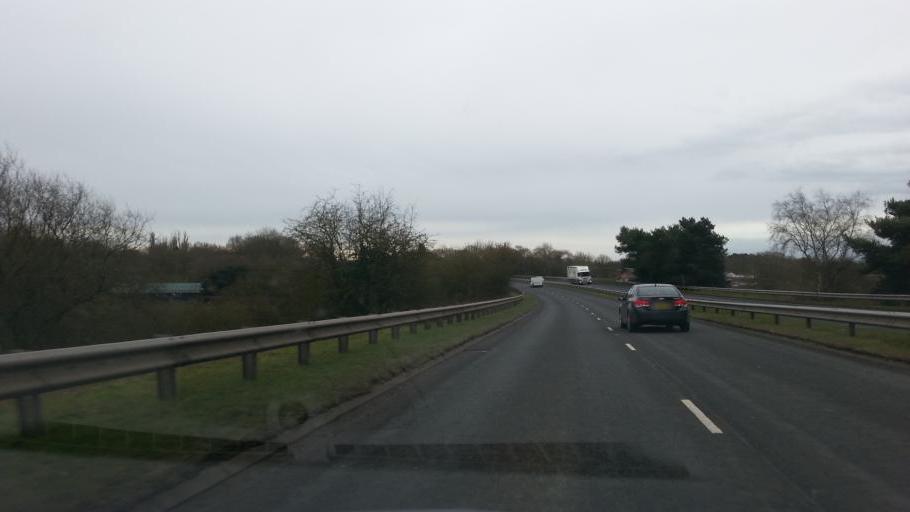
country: GB
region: England
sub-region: Solihull
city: Tidbury Green
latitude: 52.3625
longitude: -1.8894
